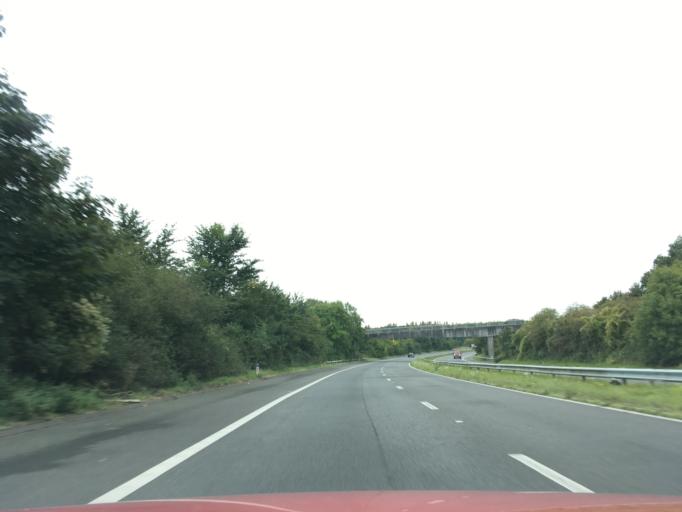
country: GB
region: Wales
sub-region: Monmouthshire
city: Caldicot
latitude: 51.6053
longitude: -2.7397
